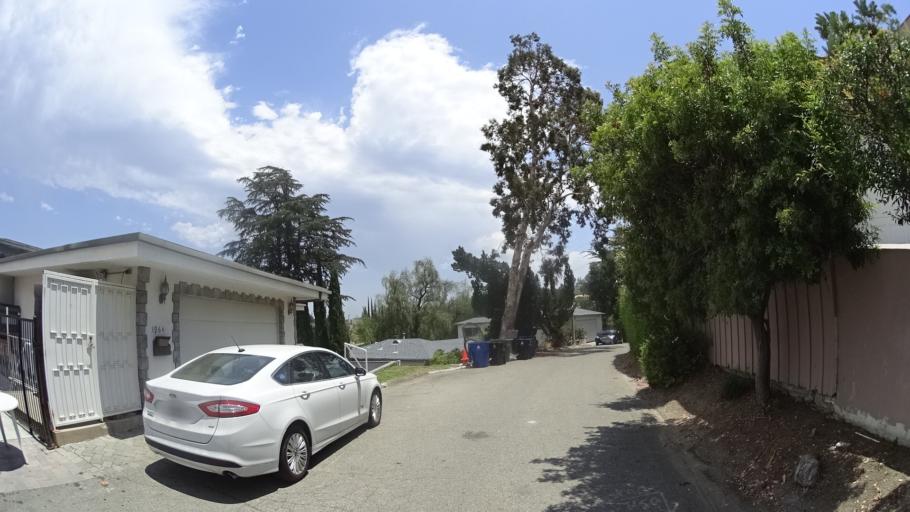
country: US
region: California
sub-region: Los Angeles County
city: Sherman Oaks
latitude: 34.1433
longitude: -118.4347
